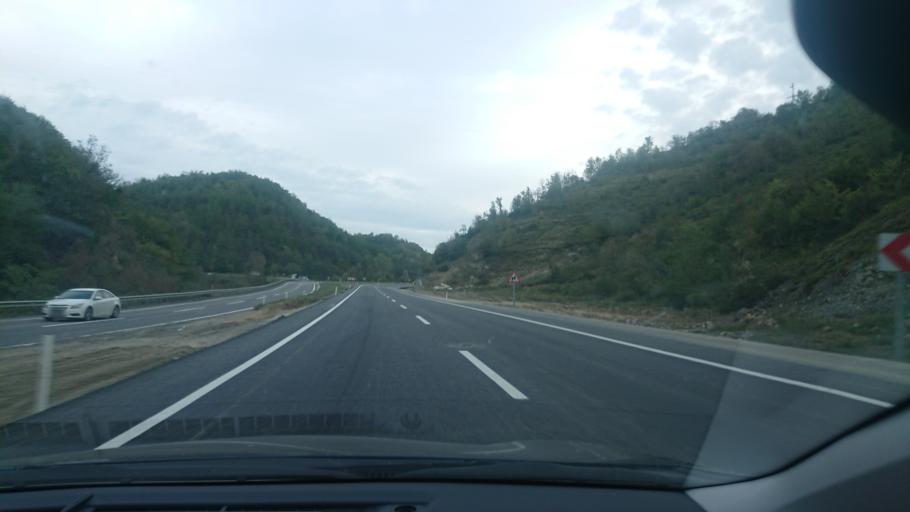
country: TR
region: Zonguldak
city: Beycuma
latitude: 41.3945
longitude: 31.9366
